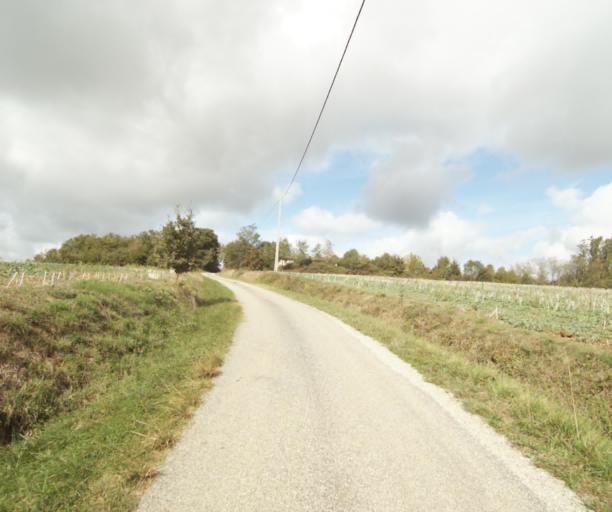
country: FR
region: Midi-Pyrenees
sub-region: Departement du Tarn-et-Garonne
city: Finhan
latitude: 43.8760
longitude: 1.1294
